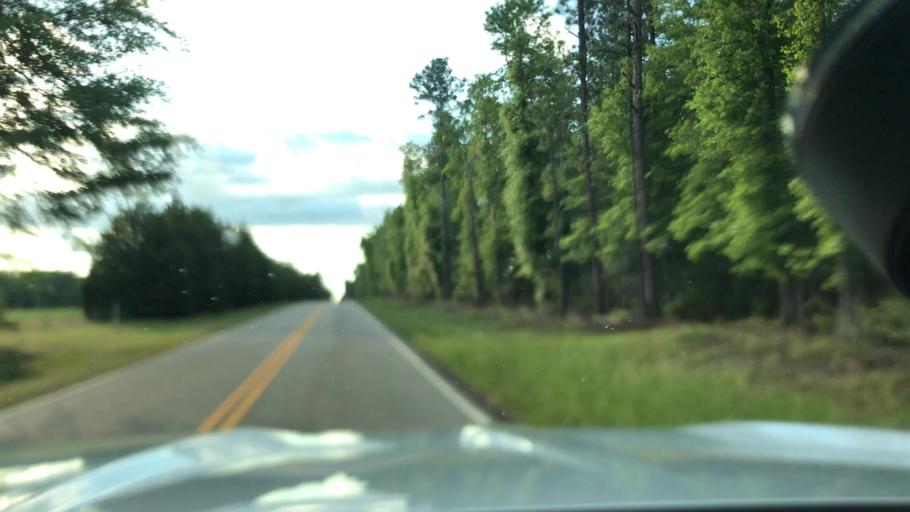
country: US
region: South Carolina
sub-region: Bamberg County
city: Denmark
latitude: 33.4543
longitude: -81.1394
